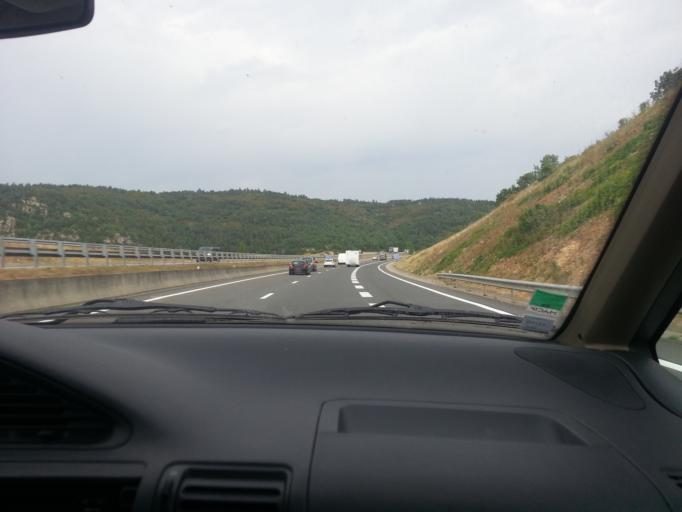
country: FR
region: Midi-Pyrenees
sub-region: Departement de l'Aveyron
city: Severac-le-Chateau
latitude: 44.3408
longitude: 3.0834
